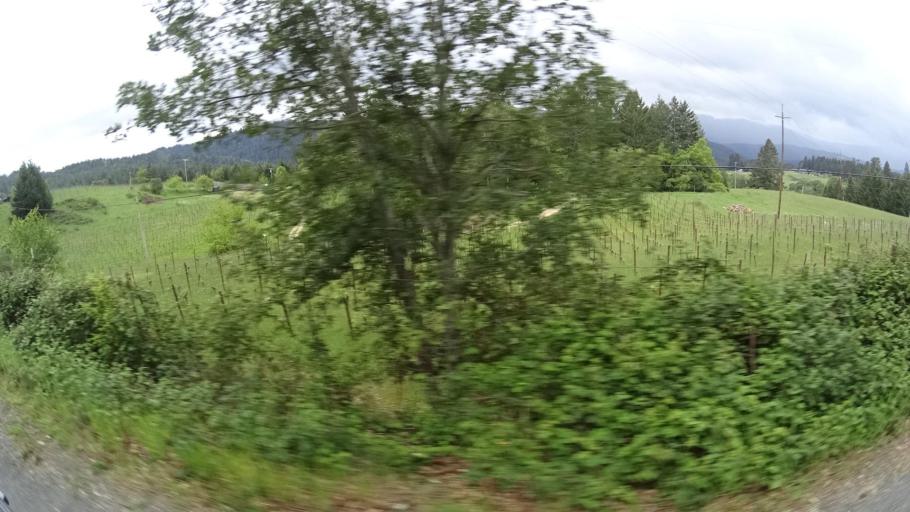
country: US
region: California
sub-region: Humboldt County
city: Redway
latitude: 40.2882
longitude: -123.8021
